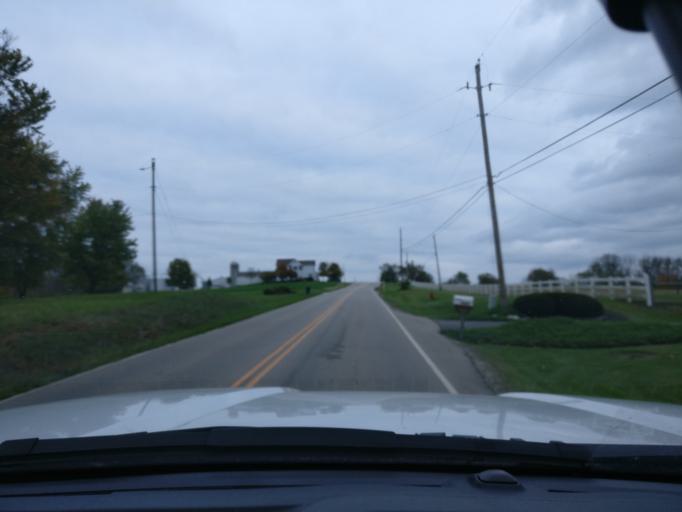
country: US
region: Ohio
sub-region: Warren County
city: Hunter
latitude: 39.4644
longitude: -84.3131
